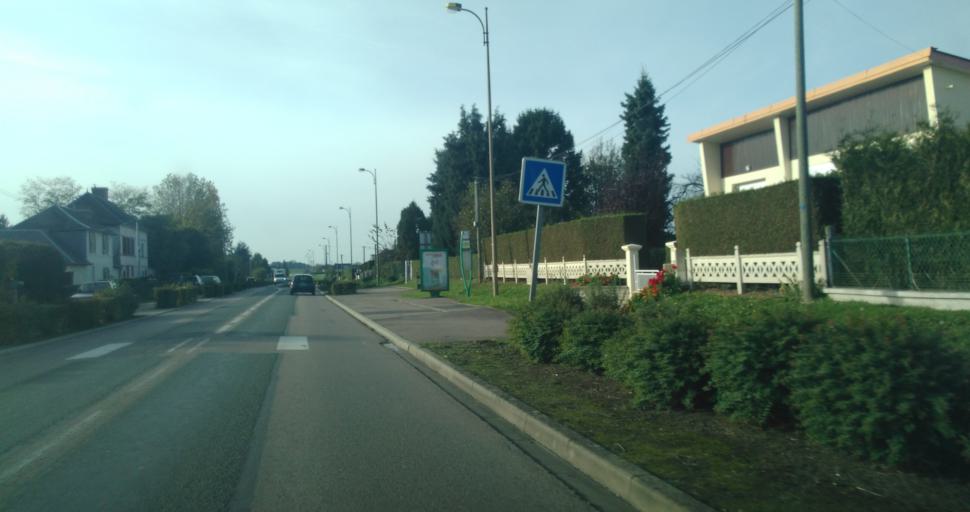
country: FR
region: Haute-Normandie
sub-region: Departement de l'Eure
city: Bourg-Achard
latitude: 49.3545
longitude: 0.8043
